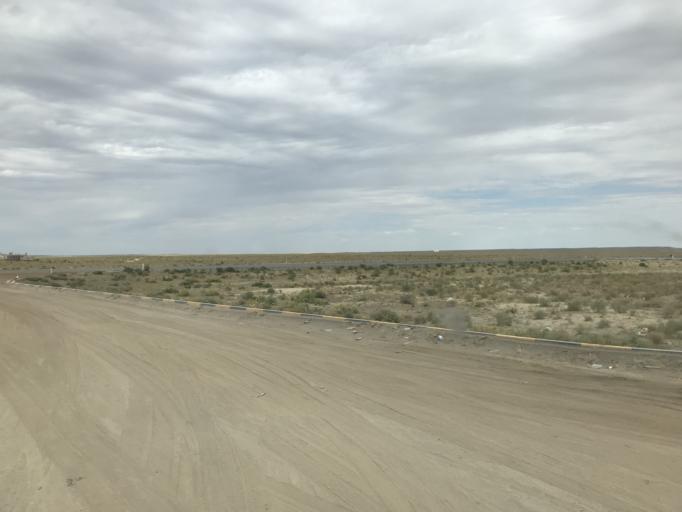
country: KZ
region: Qyzylorda
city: Aral
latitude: 46.8288
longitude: 61.6916
